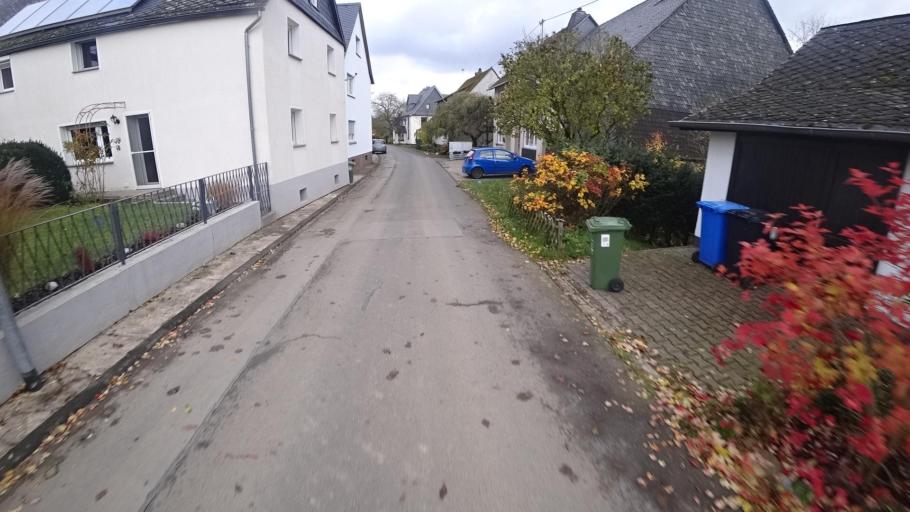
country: DE
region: Rheinland-Pfalz
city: Badenhard
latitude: 50.1225
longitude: 7.6286
